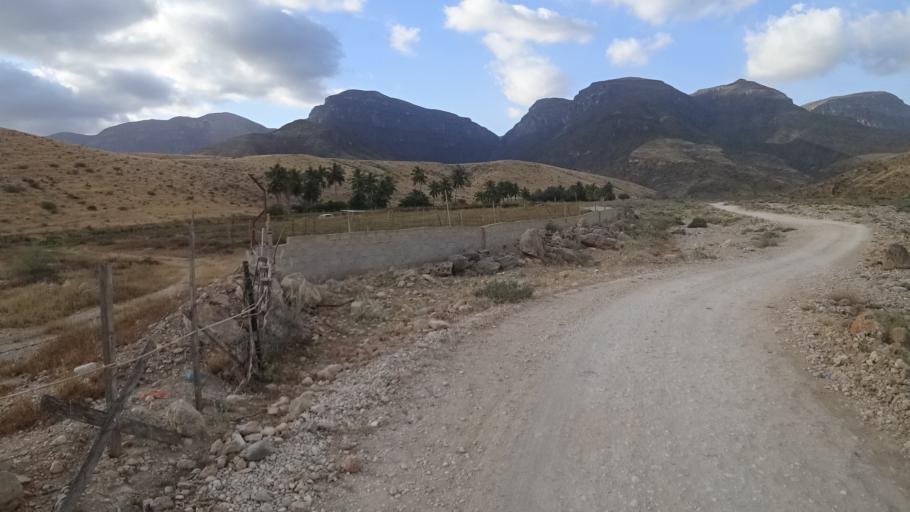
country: OM
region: Zufar
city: Salalah
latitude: 16.9886
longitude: 53.8471
